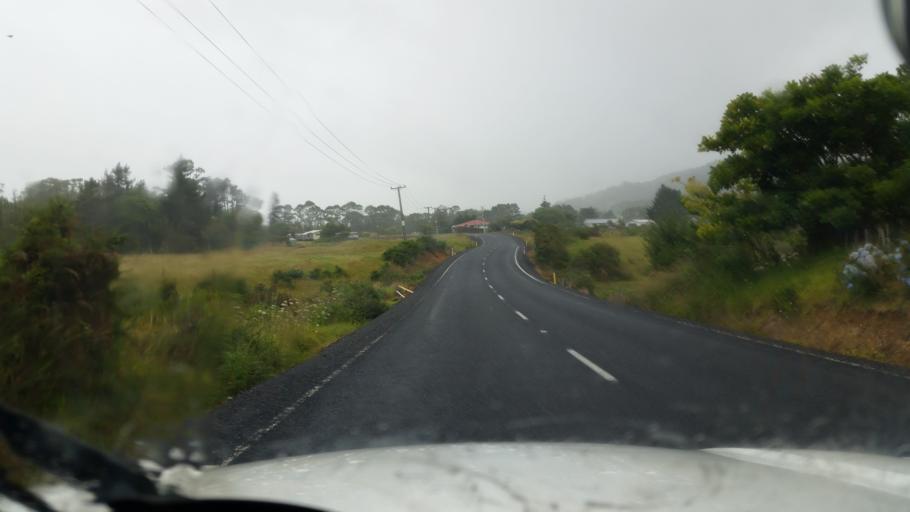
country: NZ
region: Northland
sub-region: Far North District
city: Ahipara
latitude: -35.1763
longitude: 173.1753
